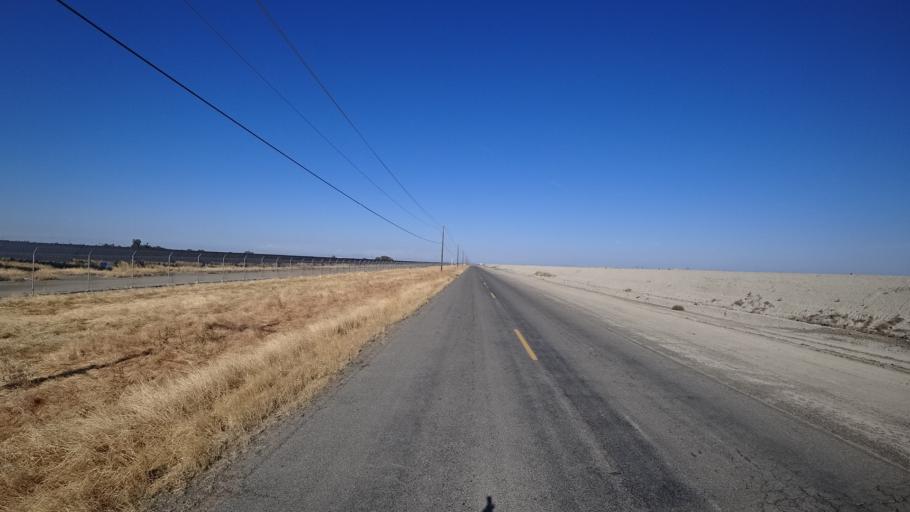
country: US
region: California
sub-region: Kings County
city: Corcoran
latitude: 36.1379
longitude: -119.5570
